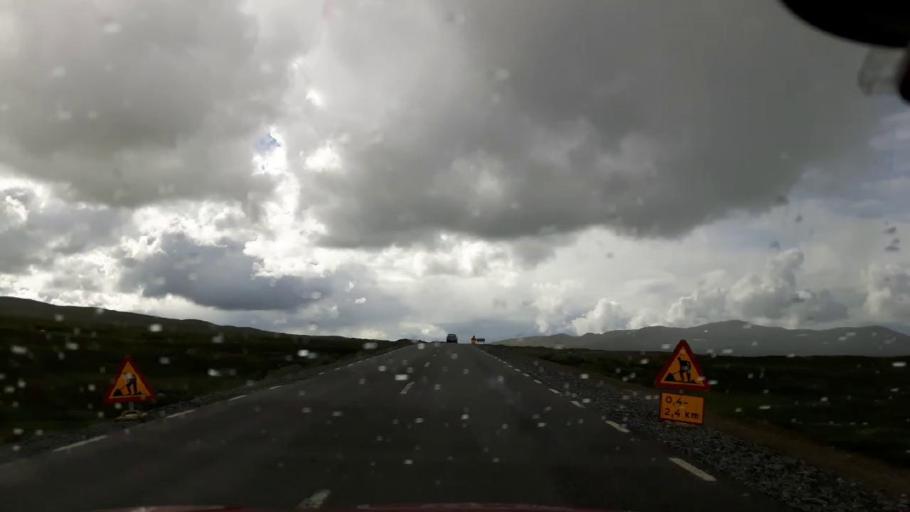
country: NO
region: Nordland
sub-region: Hattfjelldal
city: Hattfjelldal
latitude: 65.0990
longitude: 14.4675
